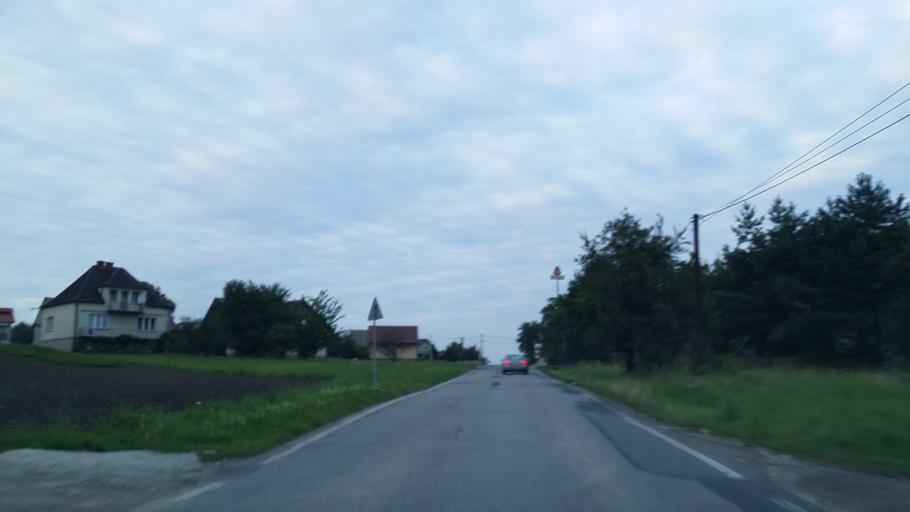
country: PL
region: Lesser Poland Voivodeship
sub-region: Powiat krakowski
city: Kaszow
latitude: 50.0136
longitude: 19.7158
